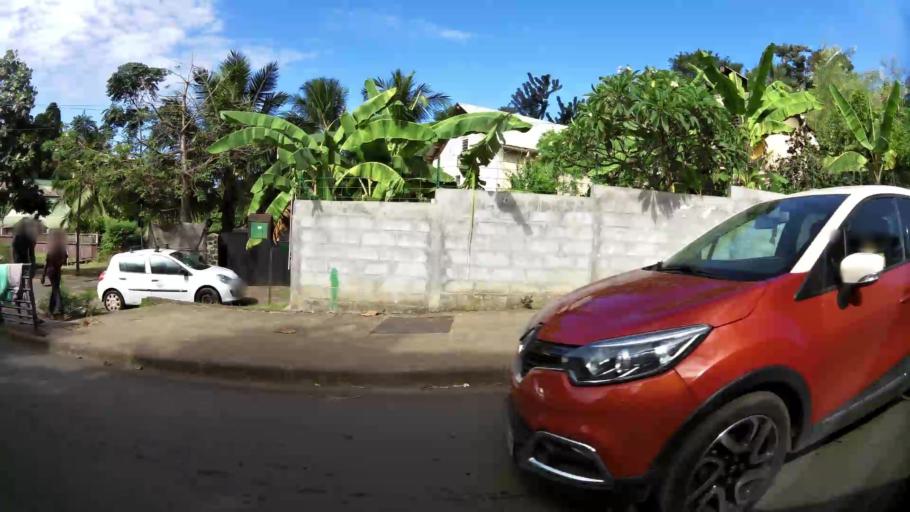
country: YT
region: Mamoudzou
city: Mamoudzou
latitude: -12.7845
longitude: 45.2229
